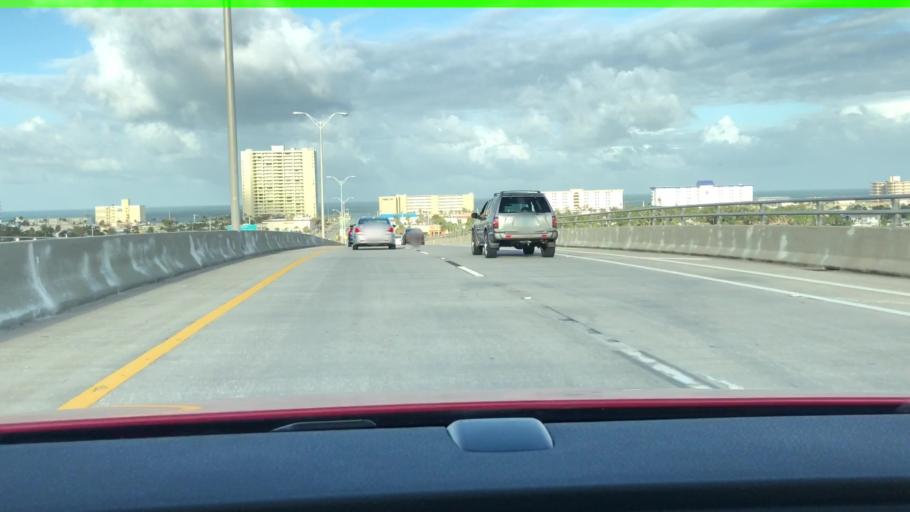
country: US
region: Florida
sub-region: Volusia County
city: Port Orange
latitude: 29.1484
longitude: -80.9750
